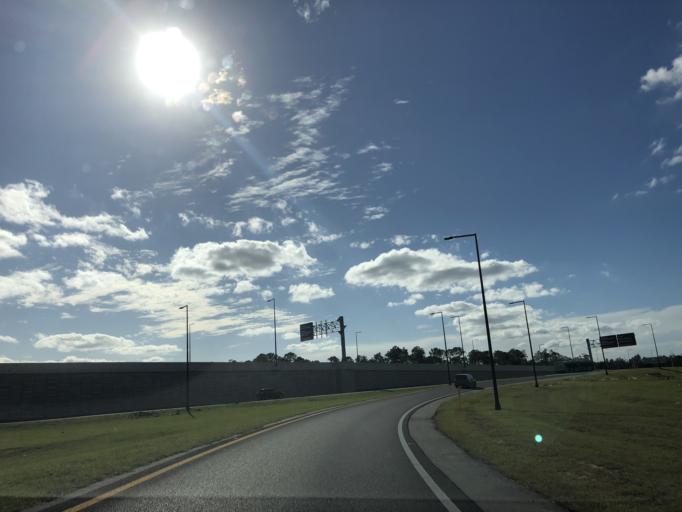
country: US
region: Florida
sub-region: Osceola County
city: Celebration
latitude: 28.3491
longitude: -81.5532
